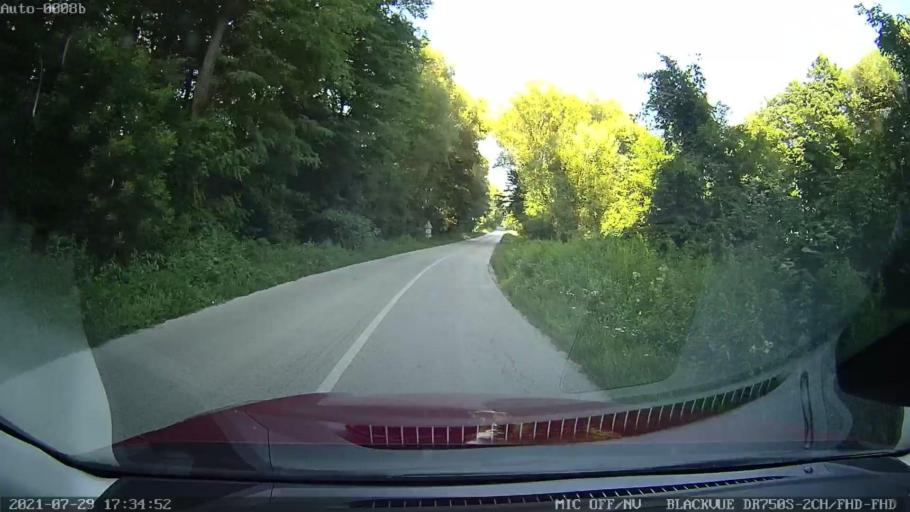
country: HR
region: Varazdinska
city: Vinica
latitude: 46.2951
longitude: 16.1485
